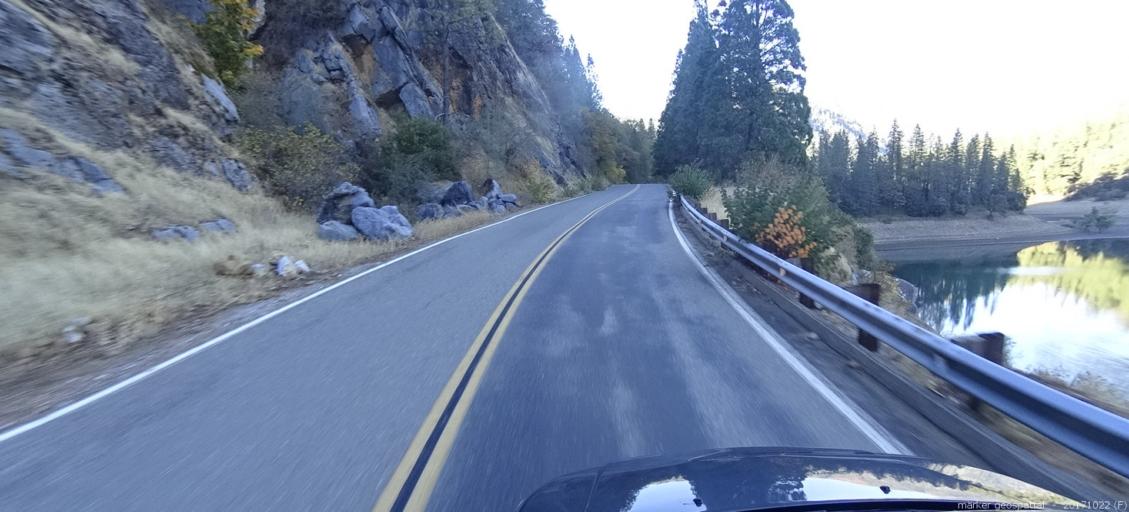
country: US
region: California
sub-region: Shasta County
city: Shasta Lake
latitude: 40.9235
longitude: -122.2478
